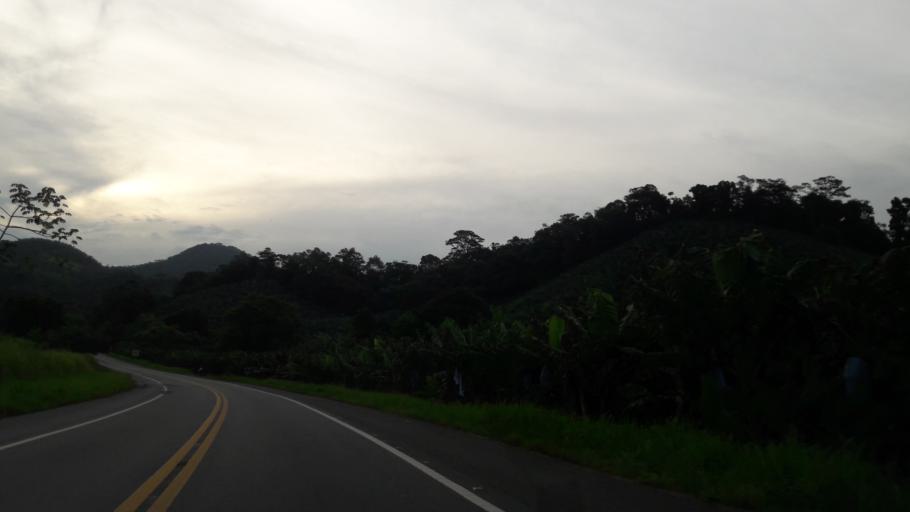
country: BR
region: Sao Paulo
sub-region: Miracatu
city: Miracatu
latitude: -24.2748
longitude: -47.2551
